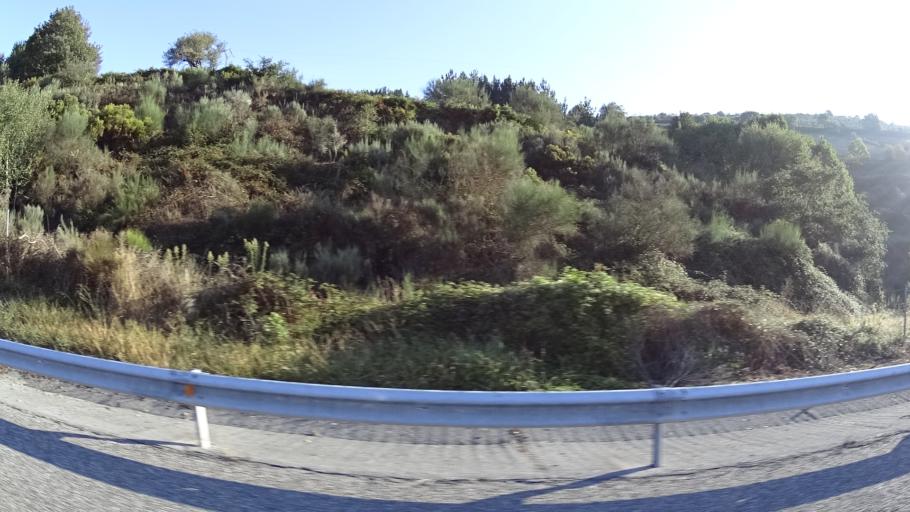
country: ES
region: Galicia
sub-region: Provincia de Lugo
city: San Roman
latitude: 42.7718
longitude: -7.0912
